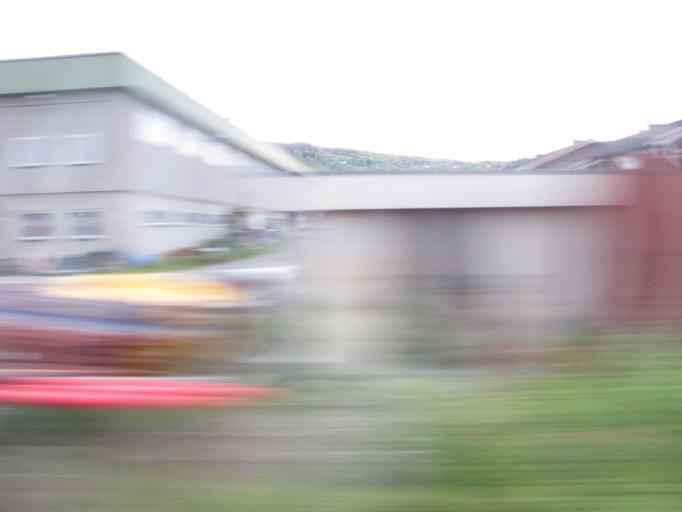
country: NO
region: Oppland
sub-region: Lillehammer
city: Lillehammer
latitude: 61.1270
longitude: 10.4445
